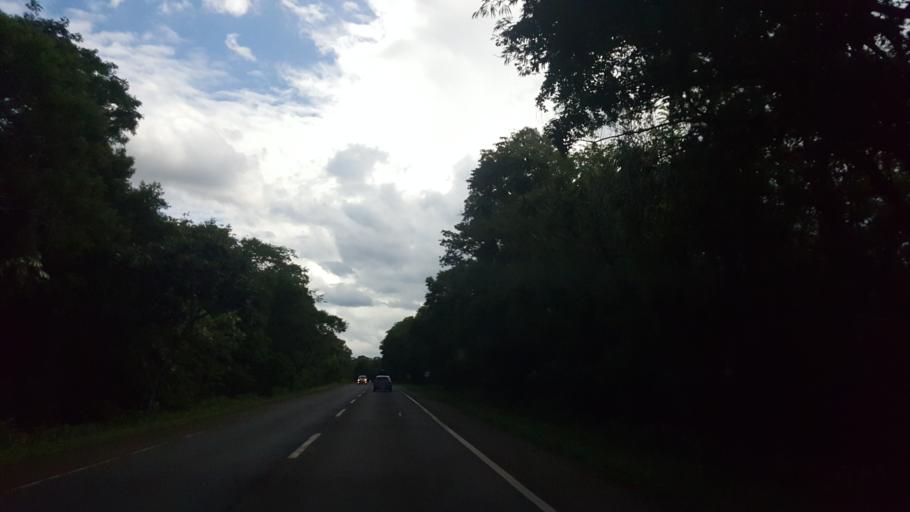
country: AR
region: Misiones
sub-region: Departamento de Iguazu
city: Puerto Iguazu
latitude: -25.6868
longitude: -54.5123
